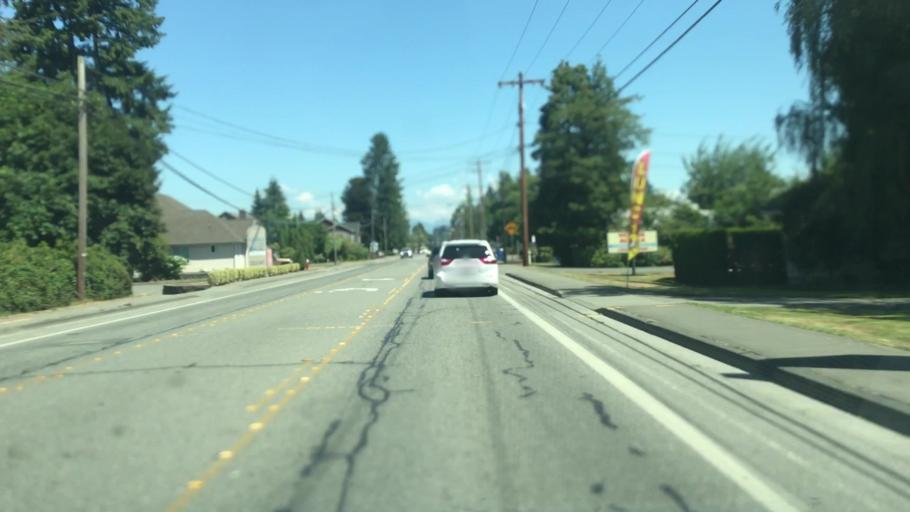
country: US
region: Washington
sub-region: Snohomish County
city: Monroe
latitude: 47.8516
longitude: -121.9838
